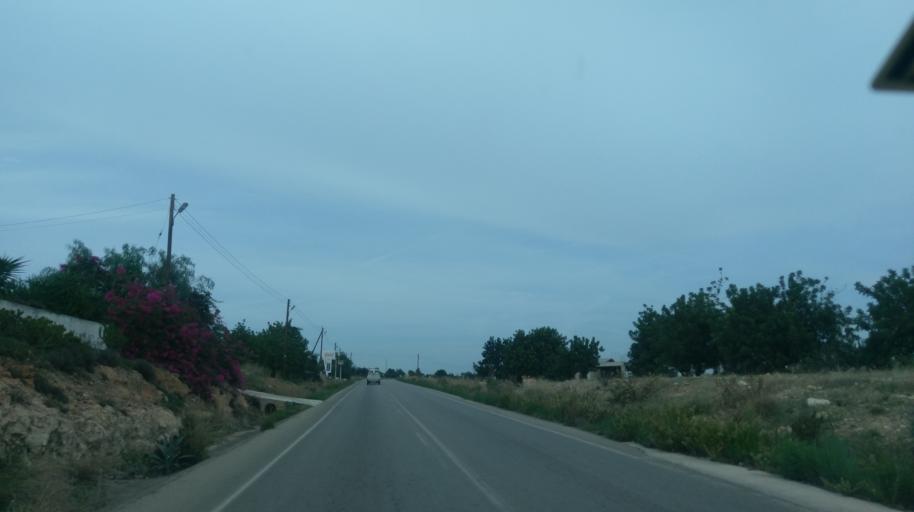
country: CY
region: Ammochostos
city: Leonarisso
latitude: 35.4216
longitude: 34.1257
